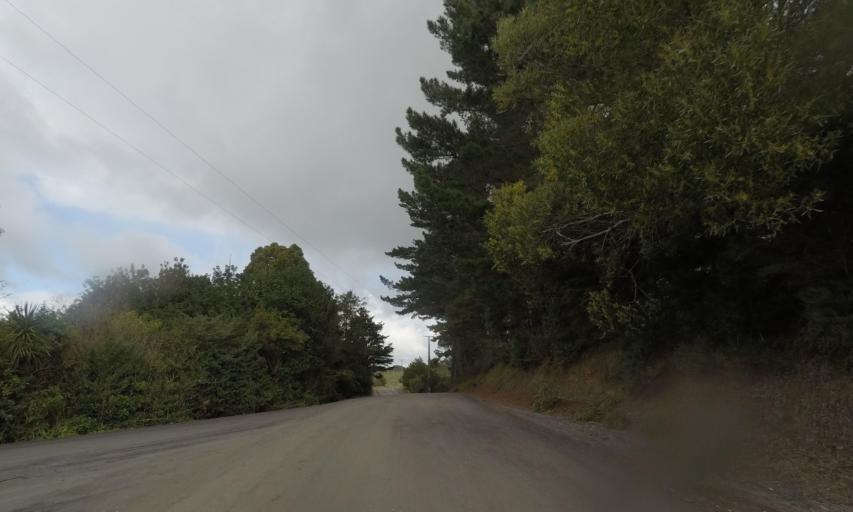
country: NZ
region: Auckland
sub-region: Auckland
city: Wellsford
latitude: -36.1711
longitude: 174.6013
